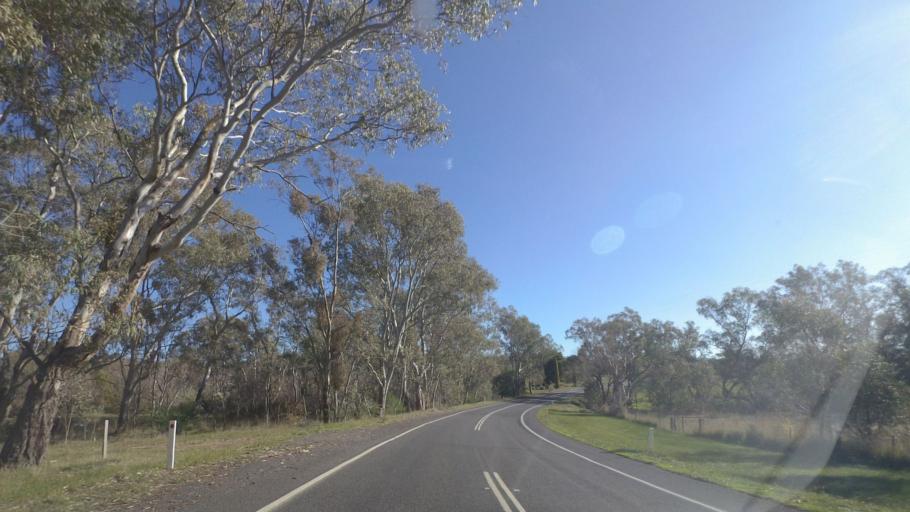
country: AU
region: Victoria
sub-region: Greater Bendigo
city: Kennington
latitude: -36.9116
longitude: 144.3180
